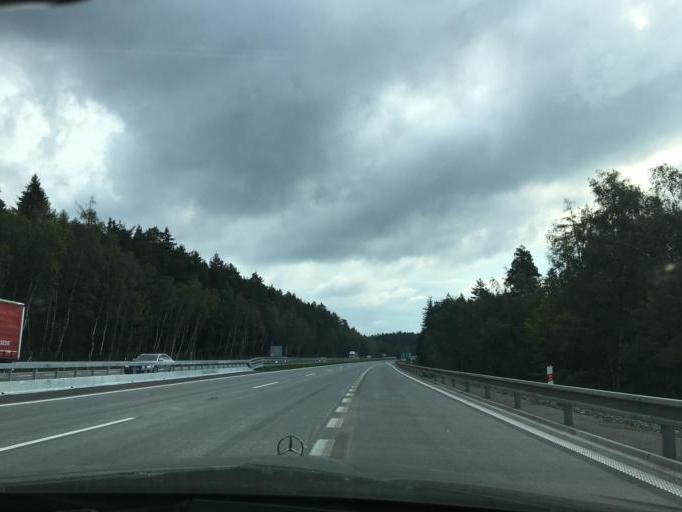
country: CZ
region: South Moravian
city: Zbraslav
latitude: 49.2696
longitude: 16.2819
